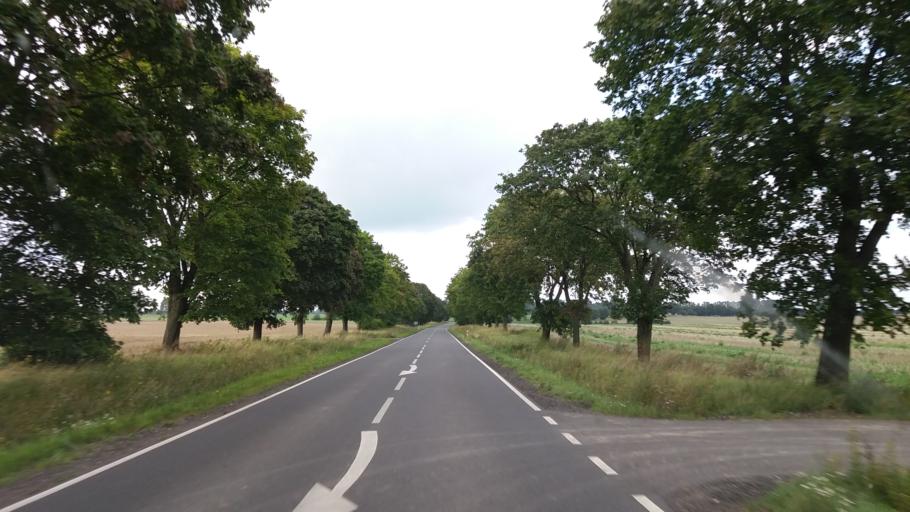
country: PL
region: West Pomeranian Voivodeship
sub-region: Powiat choszczenski
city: Choszczno
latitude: 53.1430
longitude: 15.3792
